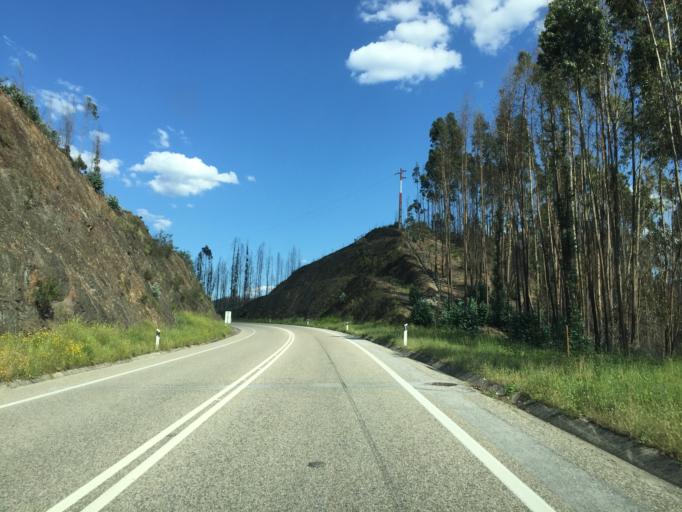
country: PT
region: Leiria
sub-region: Figueiro Dos Vinhos
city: Figueiro dos Vinhos
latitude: 39.9259
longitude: -8.3212
